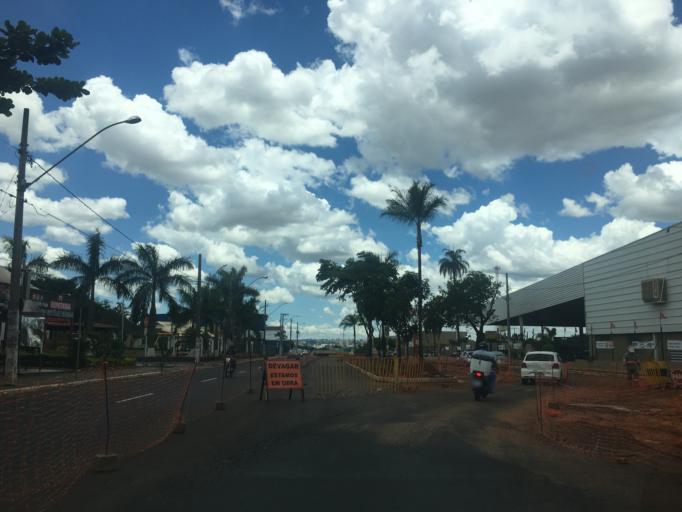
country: BR
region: Minas Gerais
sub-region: Uberlandia
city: Uberlandia
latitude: -18.9414
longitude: -48.3088
